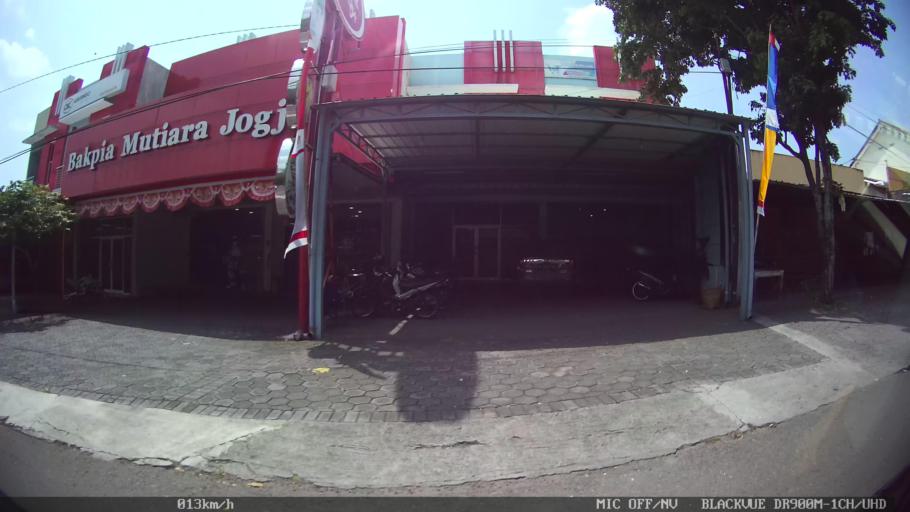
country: ID
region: Daerah Istimewa Yogyakarta
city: Yogyakarta
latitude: -7.8025
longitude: 110.3984
